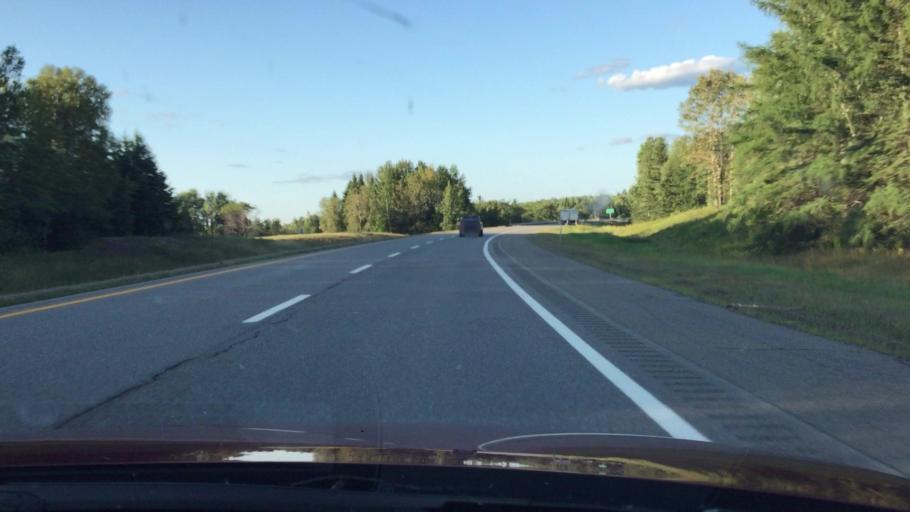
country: US
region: Maine
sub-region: Penobscot County
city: Patten
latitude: 46.0228
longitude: -68.2879
